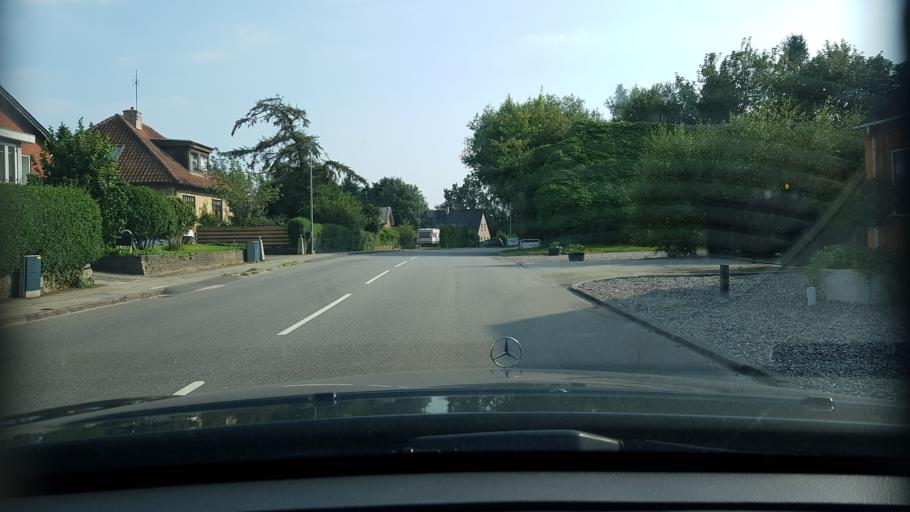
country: DK
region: North Denmark
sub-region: Mariagerfjord Kommune
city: Hadsund
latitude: 56.7593
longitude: 10.1880
